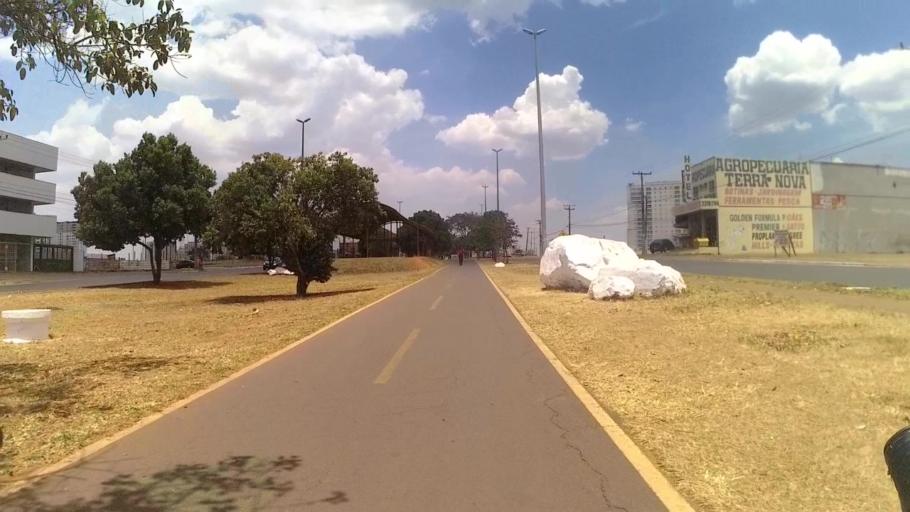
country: BR
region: Federal District
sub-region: Brasilia
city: Brasilia
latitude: -15.8761
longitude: -48.0811
